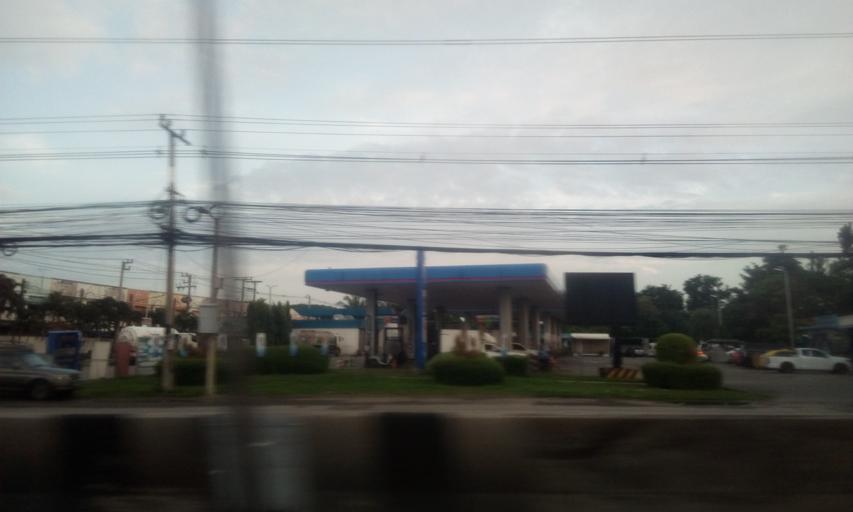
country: TH
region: Bangkok
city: Sai Mai
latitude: 13.9924
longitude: 100.6510
